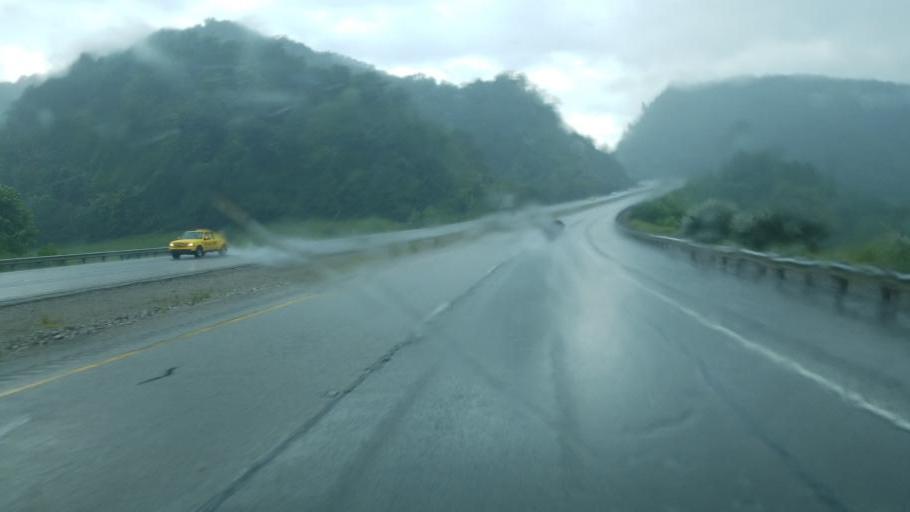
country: US
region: Kentucky
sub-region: Pike County
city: Pikeville
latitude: 37.5558
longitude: -82.4260
